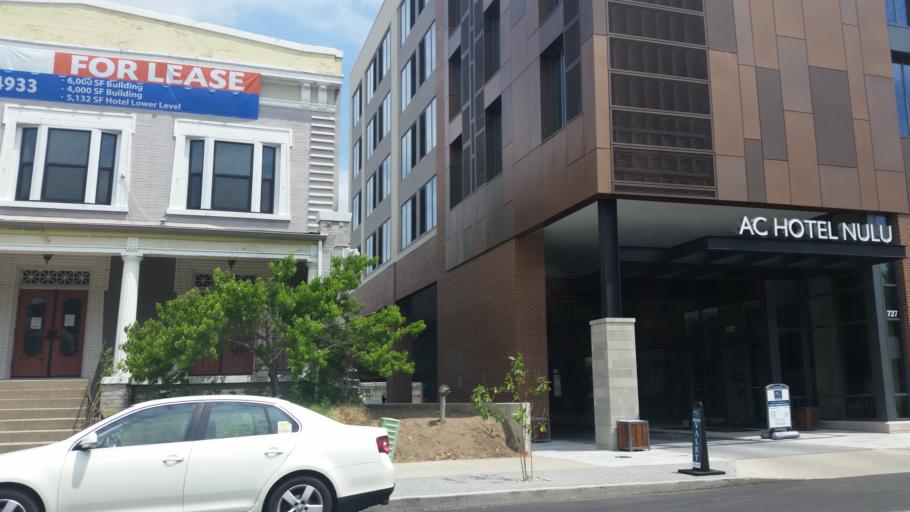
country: US
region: Kentucky
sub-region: Jefferson County
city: Louisville
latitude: 38.2534
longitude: -85.7389
